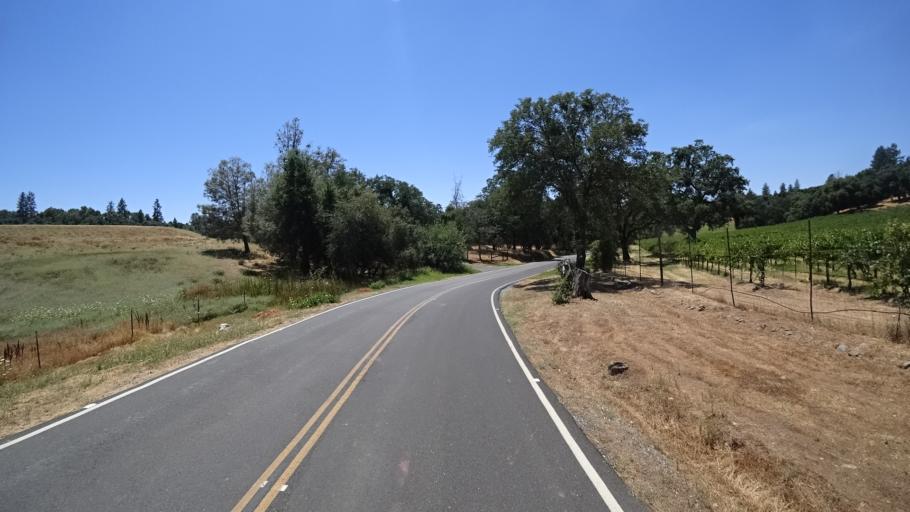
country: US
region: California
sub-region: Calaveras County
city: Murphys
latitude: 38.1253
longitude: -120.4625
